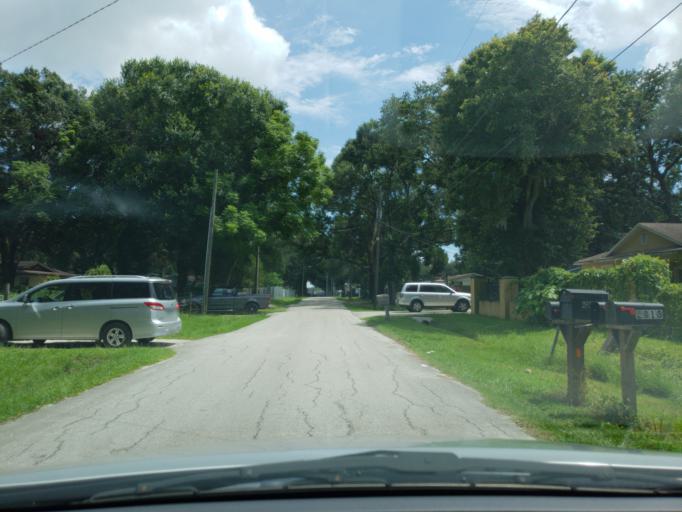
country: US
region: Florida
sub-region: Hillsborough County
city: East Lake-Orient Park
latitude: 27.9686
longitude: -82.3709
